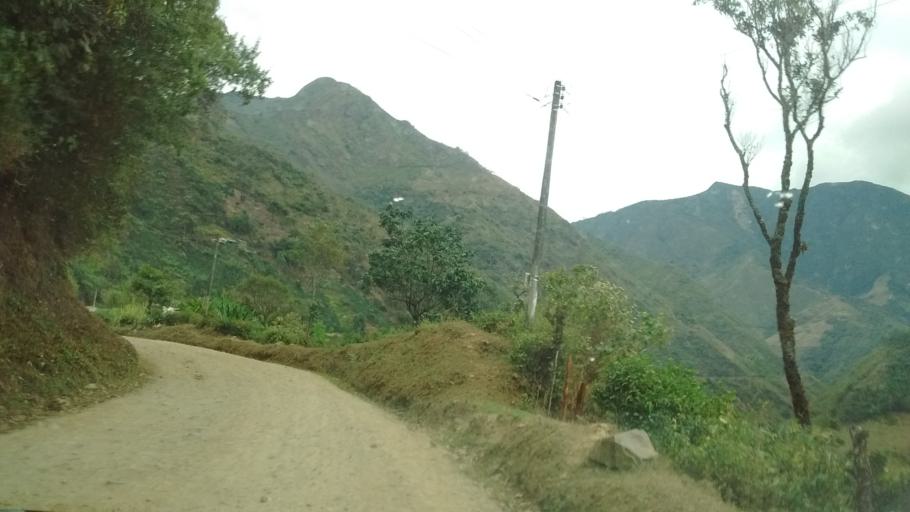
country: CO
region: Cauca
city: La Vega
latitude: 2.0424
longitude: -76.7989
